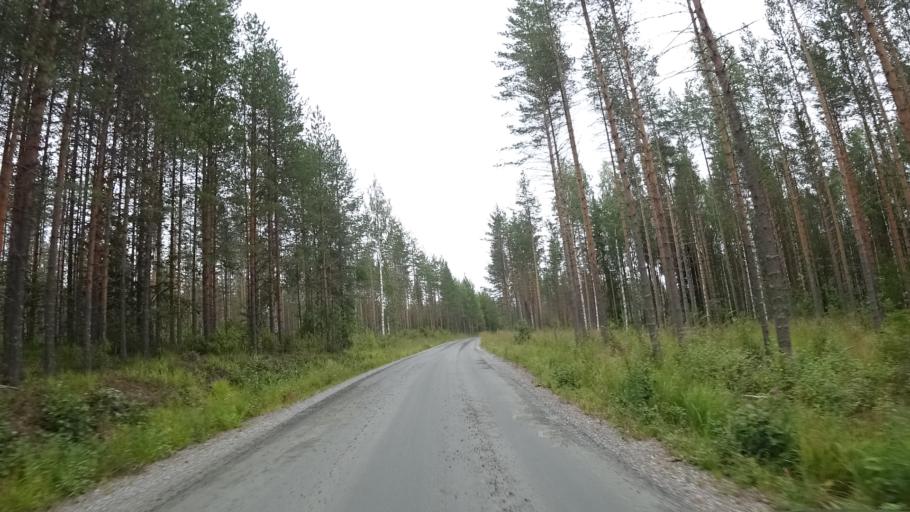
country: FI
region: North Karelia
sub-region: Pielisen Karjala
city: Lieksa
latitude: 63.3774
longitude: 30.3520
